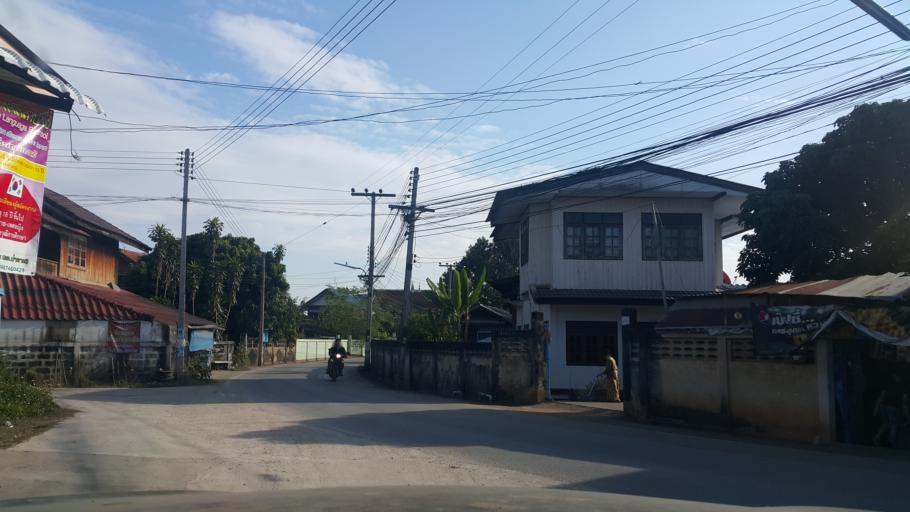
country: TH
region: Lampang
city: Hang Chat
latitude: 18.3115
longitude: 99.3532
